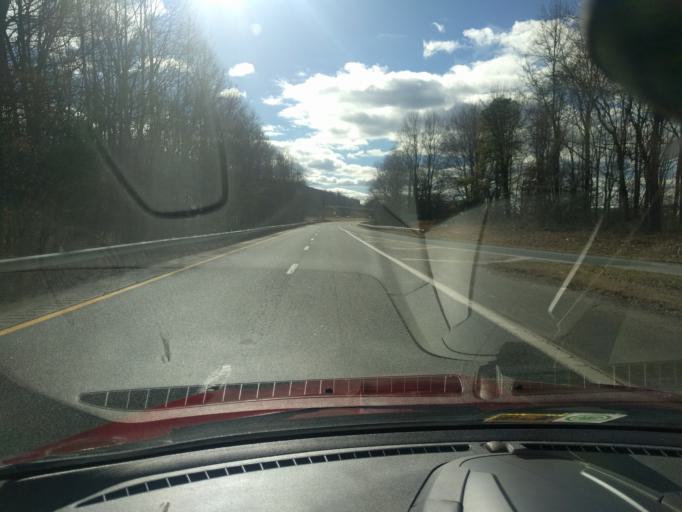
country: US
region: Virginia
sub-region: City of Lynchburg
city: West Lynchburg
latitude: 37.3601
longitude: -79.1671
